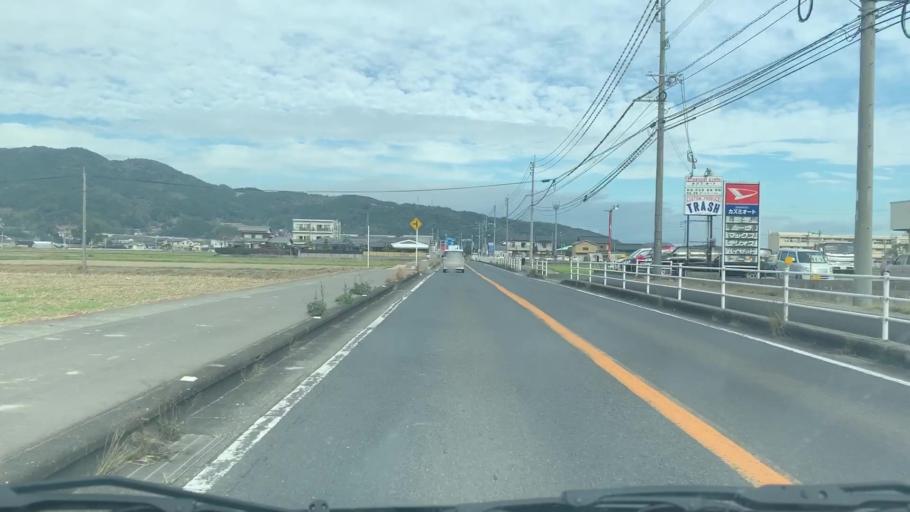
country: JP
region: Saga Prefecture
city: Karatsu
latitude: 33.4023
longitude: 129.9868
